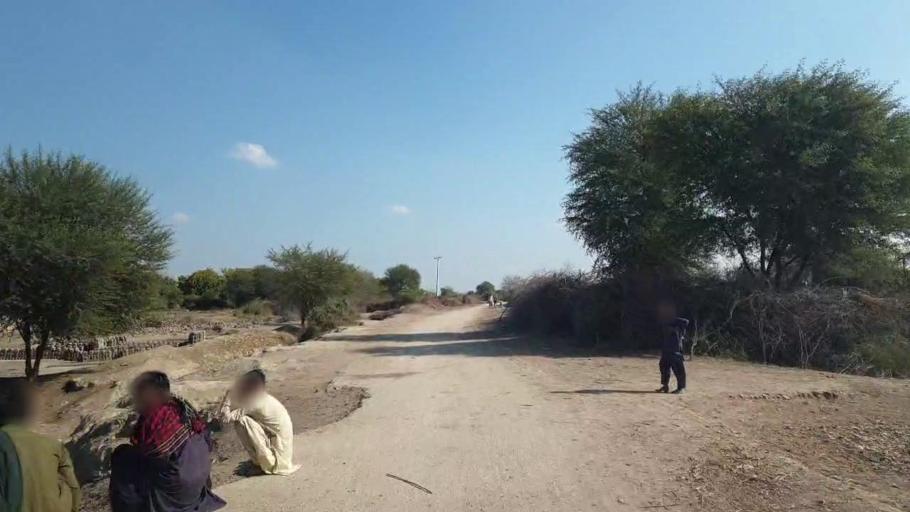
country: PK
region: Sindh
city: Shahpur Chakar
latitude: 26.0882
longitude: 68.5796
